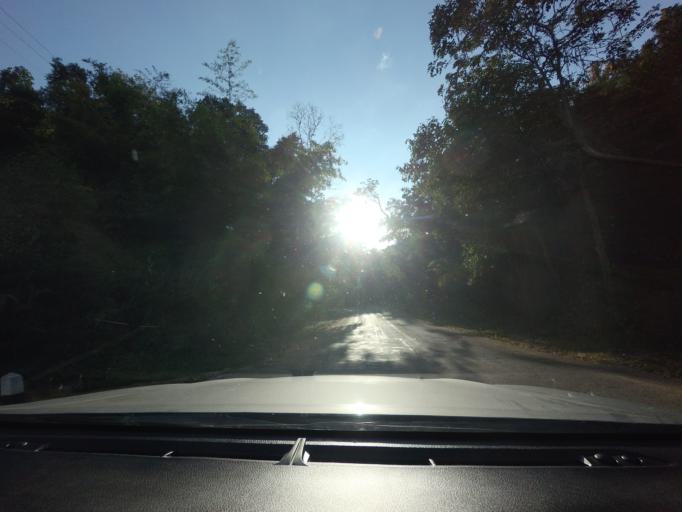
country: TH
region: Chiang Mai
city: Chai Prakan
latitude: 19.6187
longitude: 99.1644
